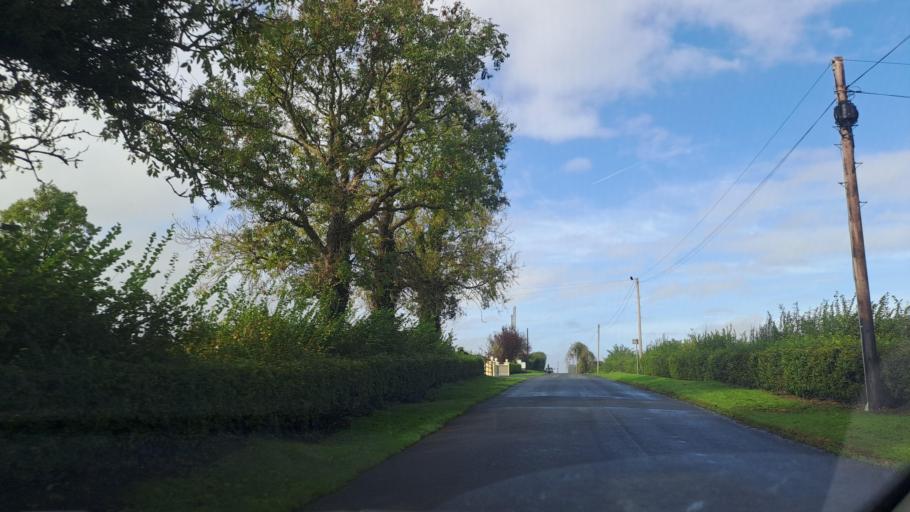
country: IE
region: Ulster
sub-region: County Monaghan
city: Carrickmacross
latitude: 53.8671
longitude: -6.6612
